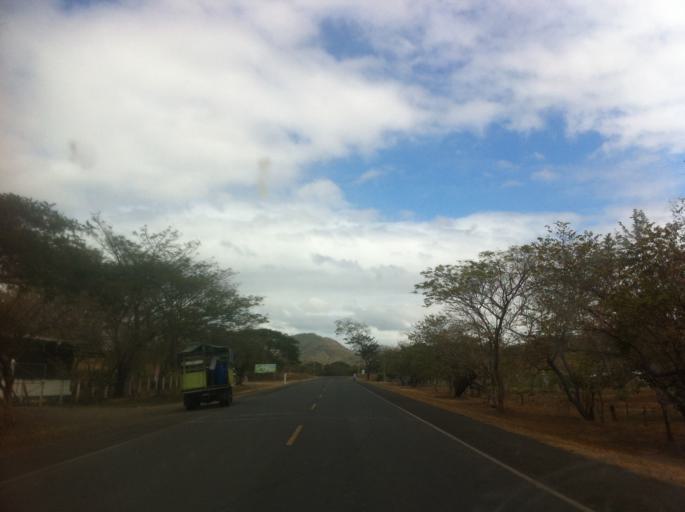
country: NI
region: Chontales
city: Acoyapa
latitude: 11.9837
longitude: -85.1698
